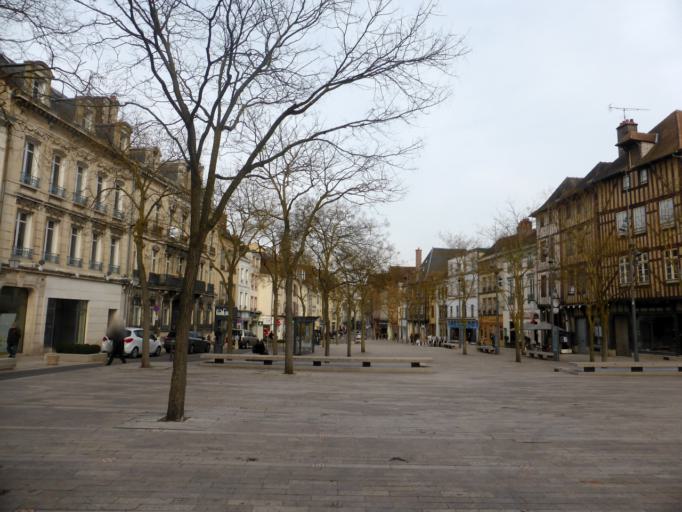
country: FR
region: Champagne-Ardenne
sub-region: Departement de l'Aube
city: Troyes
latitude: 48.2945
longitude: 4.0699
